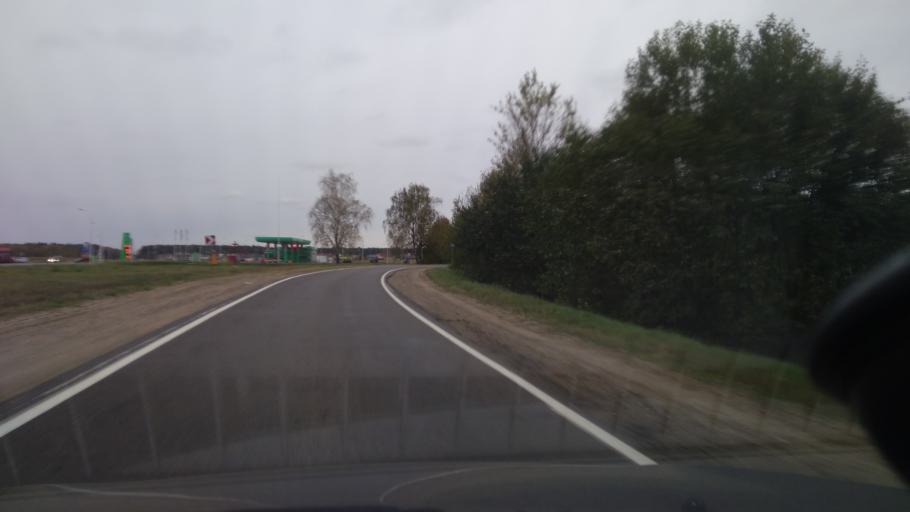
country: BY
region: Minsk
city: Dukora
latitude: 53.6577
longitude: 27.9455
